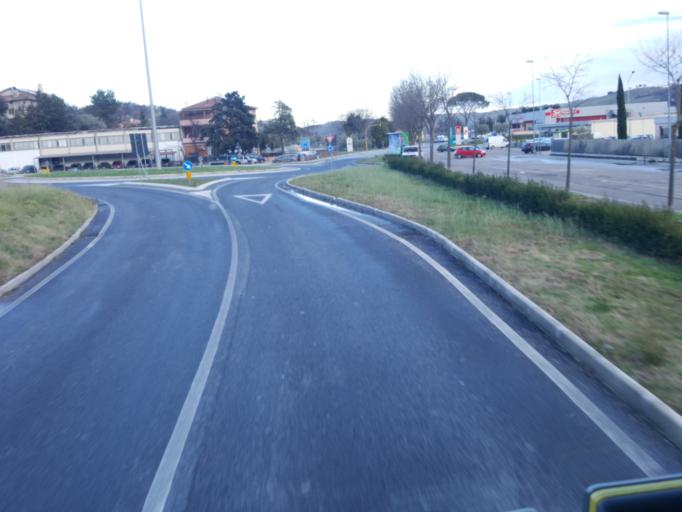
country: IT
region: The Marches
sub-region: Provincia di Macerata
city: San Severino Marche
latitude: 43.2352
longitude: 13.1897
